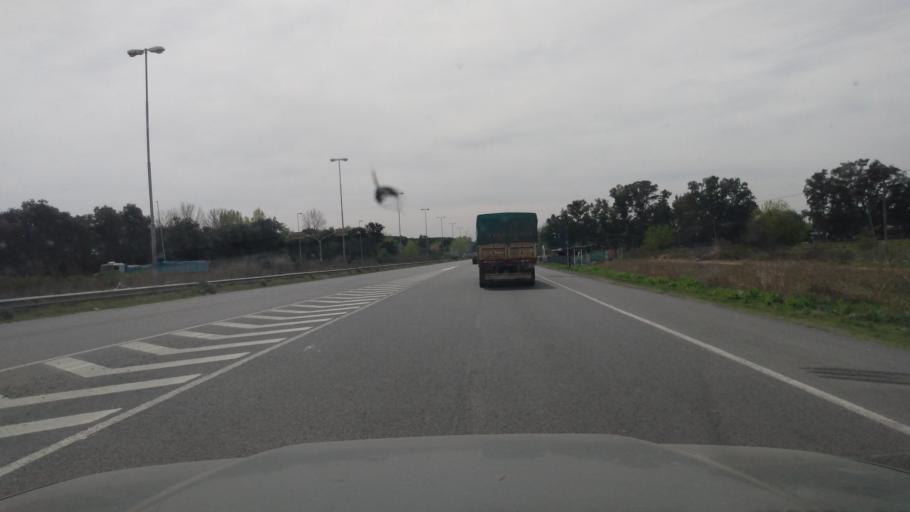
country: AR
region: Buenos Aires
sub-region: Partido de Lujan
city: Lujan
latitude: -34.4696
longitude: -59.0675
